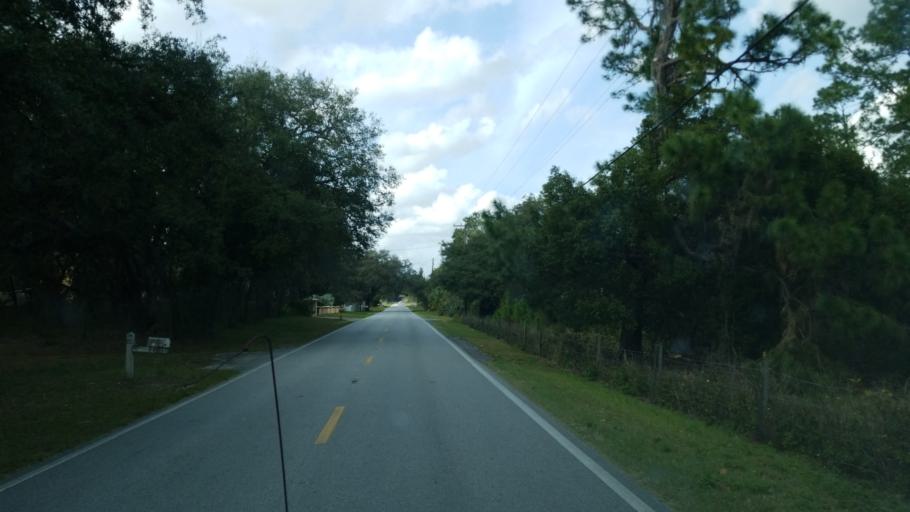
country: US
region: Florida
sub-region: Polk County
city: Davenport
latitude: 28.2025
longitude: -81.5960
